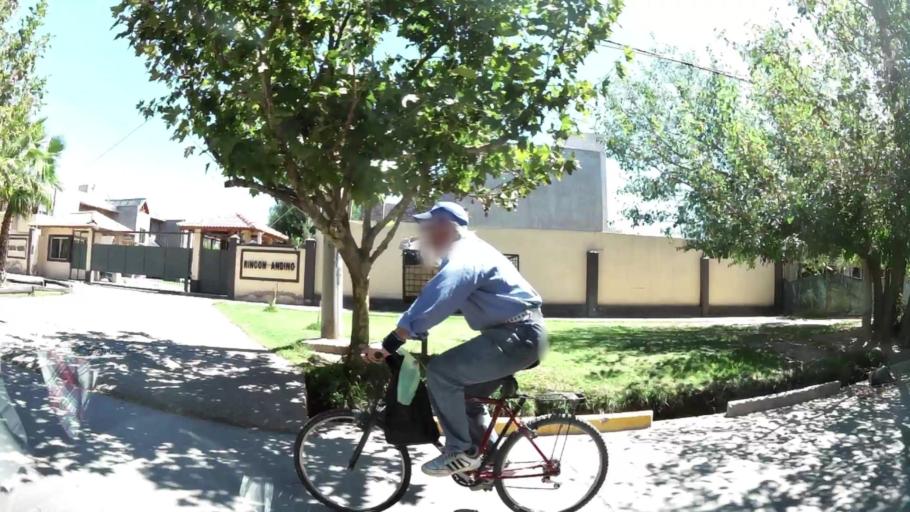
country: AR
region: Mendoza
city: Las Heras
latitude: -32.8467
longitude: -68.8468
